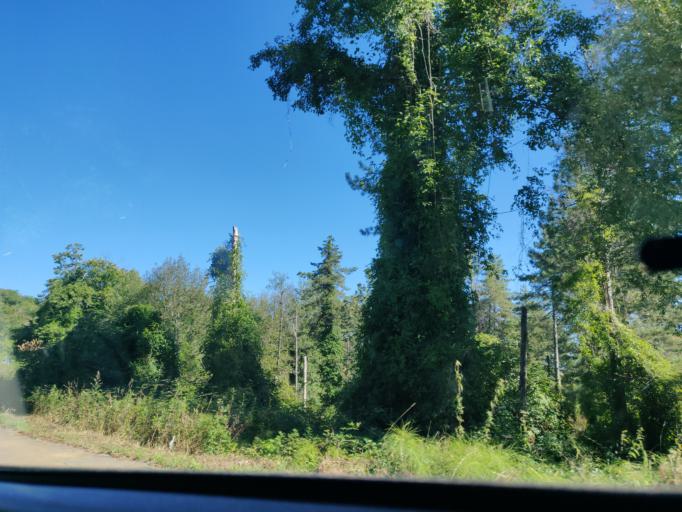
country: IT
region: Tuscany
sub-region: Provincia di Siena
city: Piancastagnaio
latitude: 42.8604
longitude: 11.6782
